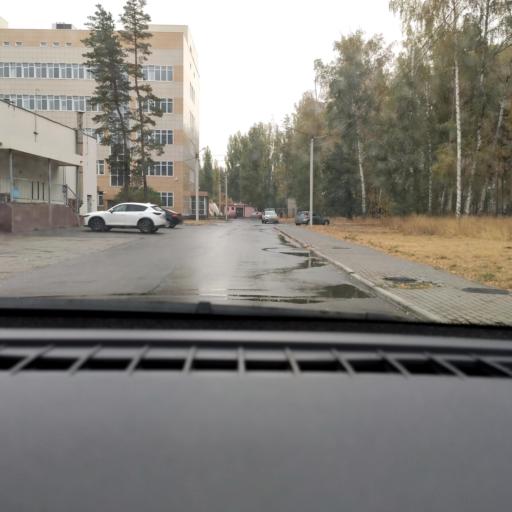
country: RU
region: Voronezj
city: Podgornoye
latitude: 51.7403
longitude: 39.1755
